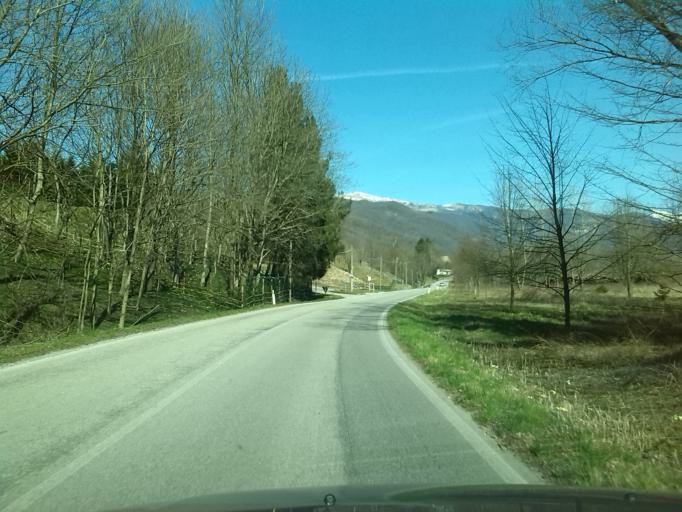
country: IT
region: Friuli Venezia Giulia
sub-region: Provincia di Udine
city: San Pietro al Natisone
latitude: 46.1259
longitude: 13.4963
